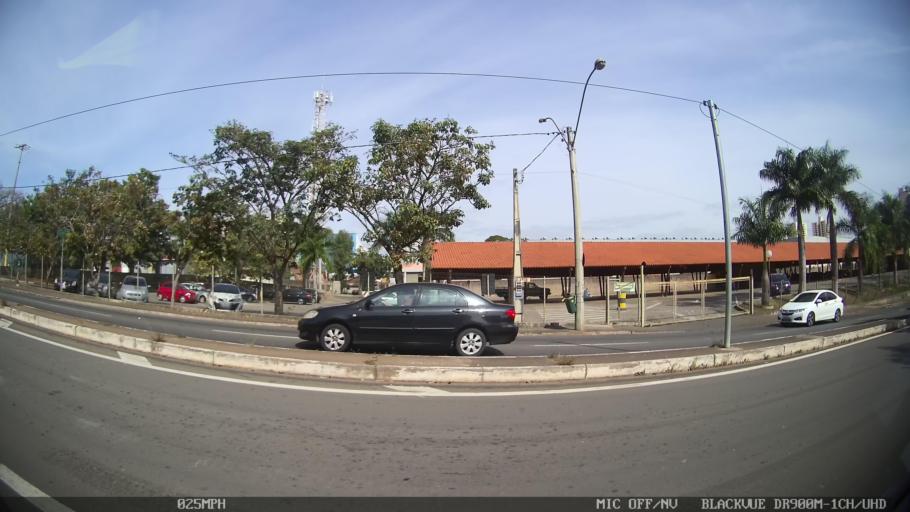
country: BR
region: Sao Paulo
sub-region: Piracicaba
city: Piracicaba
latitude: -22.7379
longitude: -47.6499
